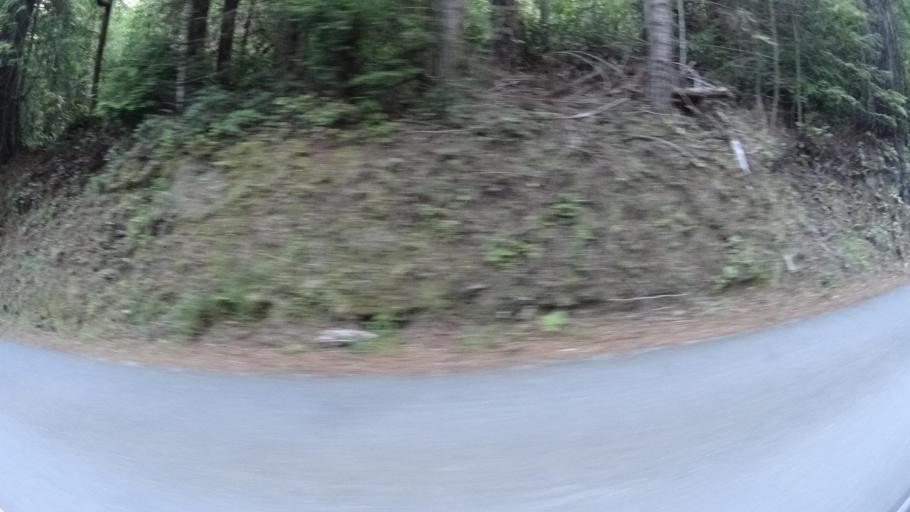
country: US
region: California
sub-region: Humboldt County
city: Bayside
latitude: 40.7589
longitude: -124.0216
